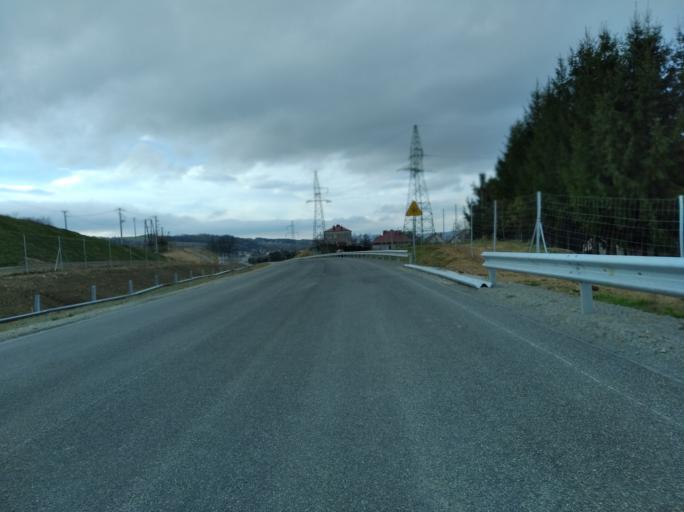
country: PL
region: Subcarpathian Voivodeship
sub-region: Powiat strzyzowski
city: Strzyzow
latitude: 49.8623
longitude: 21.8047
